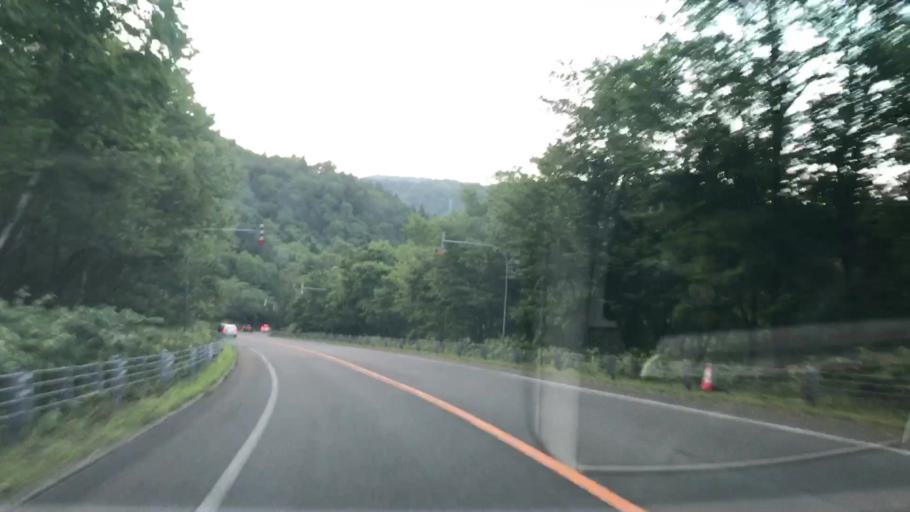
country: JP
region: Hokkaido
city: Sapporo
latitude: 42.9212
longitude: 141.1247
